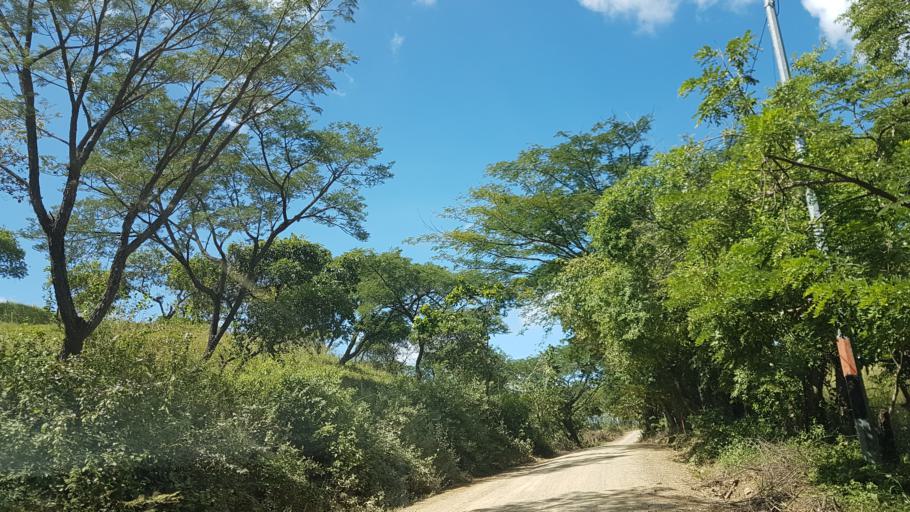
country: HN
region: El Paraiso
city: Santa Cruz
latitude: 13.7330
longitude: -86.6945
